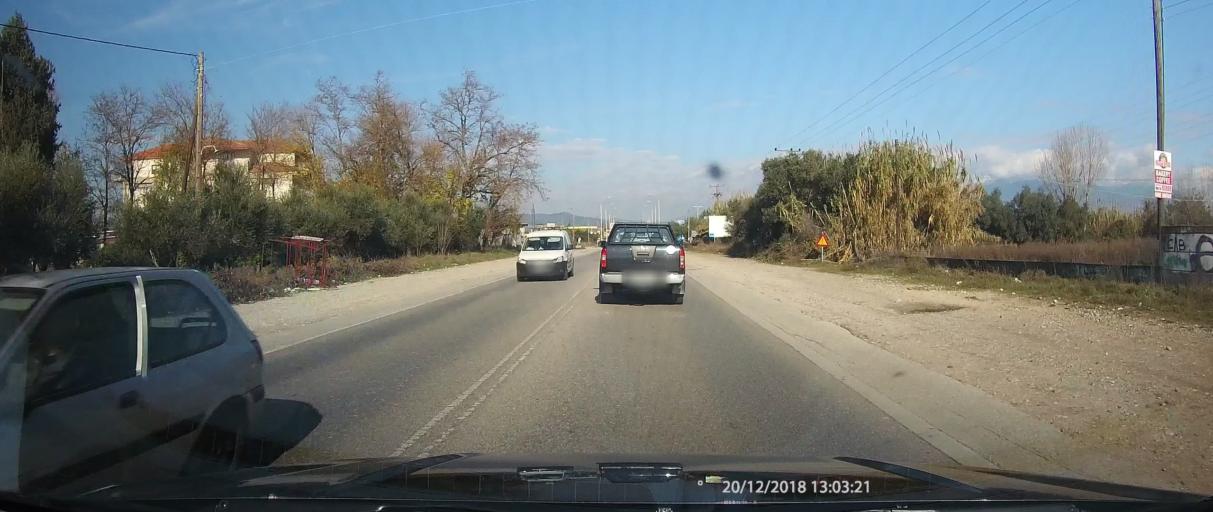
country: GR
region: West Greece
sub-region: Nomos Aitolias kai Akarnanias
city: Panaitolion
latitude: 38.5804
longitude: 21.4263
